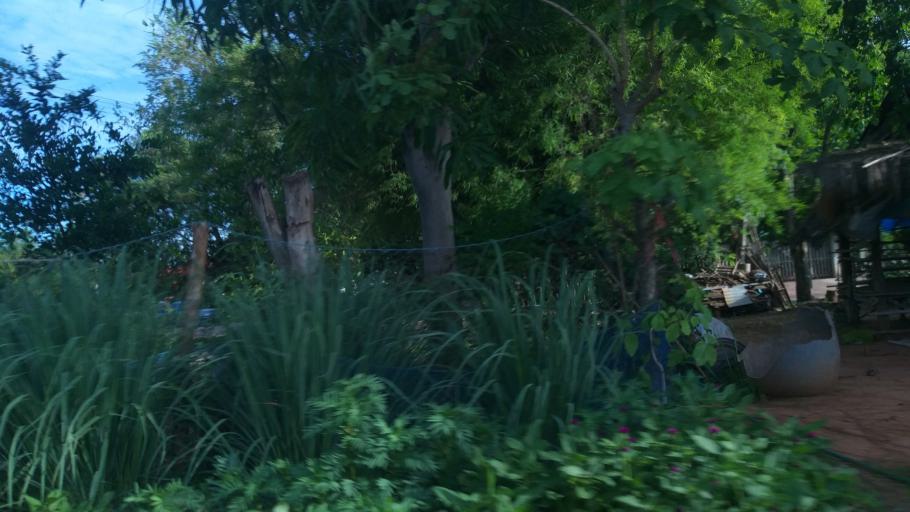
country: TH
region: Chaiyaphum
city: Ban Thaen
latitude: 16.4089
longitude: 102.3479
